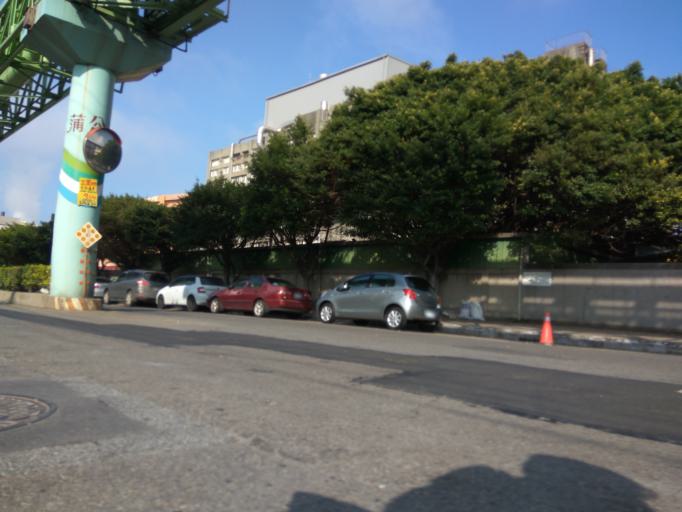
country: TW
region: Taiwan
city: Taoyuan City
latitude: 25.0741
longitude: 121.1765
